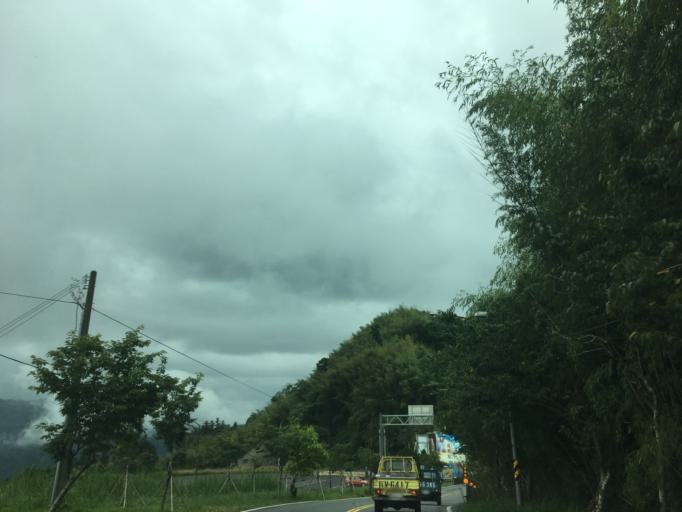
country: TW
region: Taiwan
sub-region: Chiayi
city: Jiayi Shi
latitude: 23.4640
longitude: 120.6894
